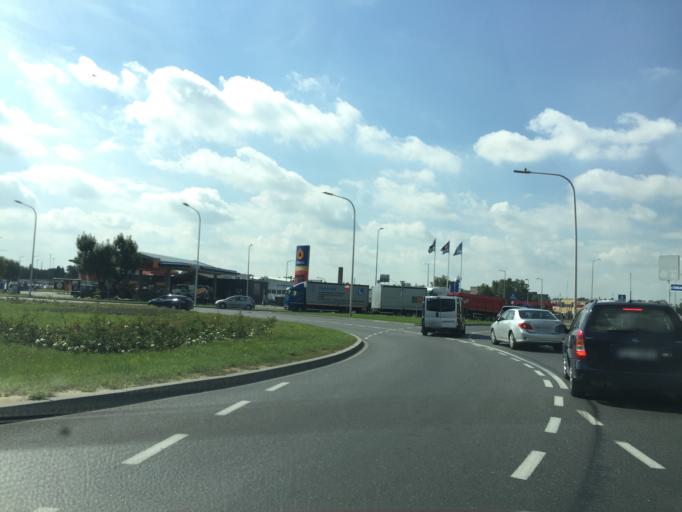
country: PL
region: Greater Poland Voivodeship
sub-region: Kalisz
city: Kalisz
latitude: 51.7489
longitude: 18.0632
